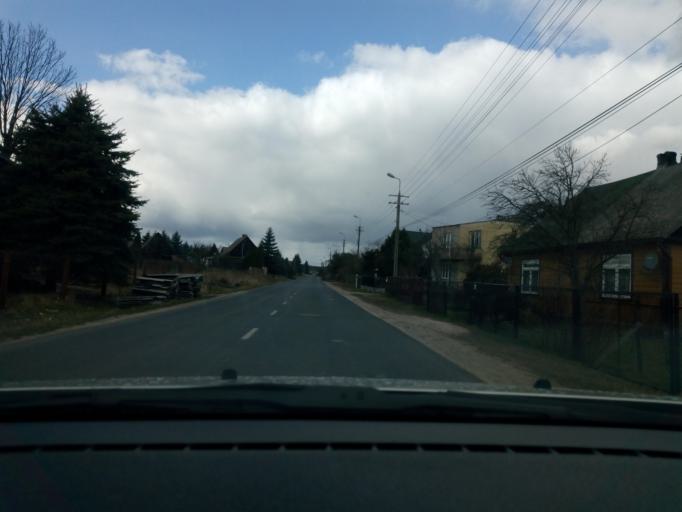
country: PL
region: Swietokrzyskie
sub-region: Powiat skarzyski
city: Skarzysko-Kamienna
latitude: 51.1511
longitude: 20.8665
